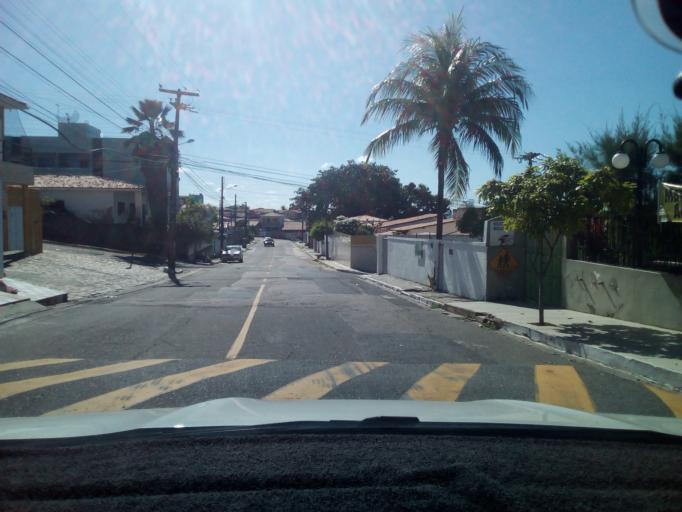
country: BR
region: Paraiba
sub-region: Joao Pessoa
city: Joao Pessoa
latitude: -7.1077
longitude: -34.8667
